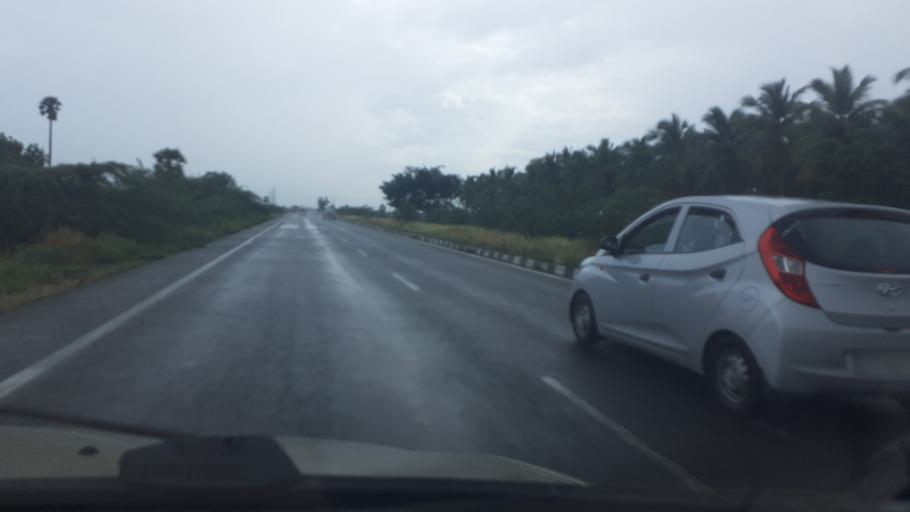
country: IN
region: Tamil Nadu
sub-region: Thoothukkudi
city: Kayattar
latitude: 8.9496
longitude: 77.7674
